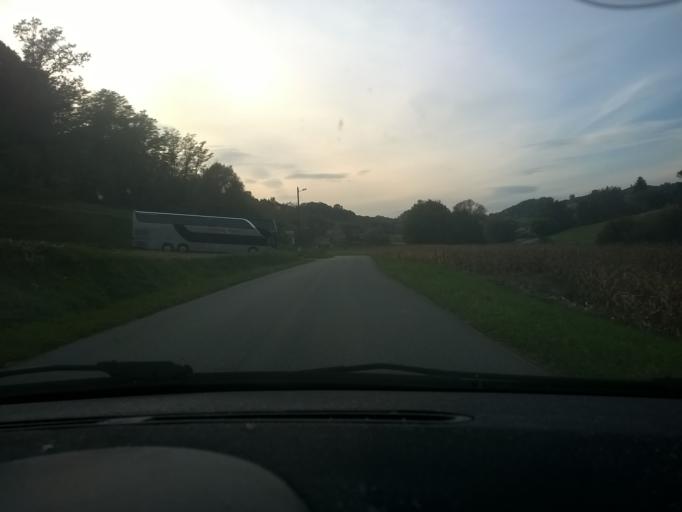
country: HR
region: Krapinsko-Zagorska
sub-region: Grad Krapina
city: Krapina
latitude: 46.1227
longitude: 15.8532
